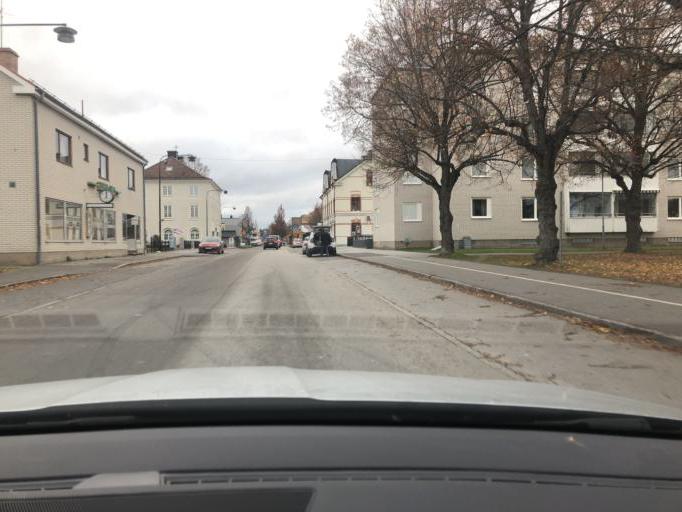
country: SE
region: Uppsala
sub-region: Tierps Kommun
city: Tierp
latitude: 60.3427
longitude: 17.5168
